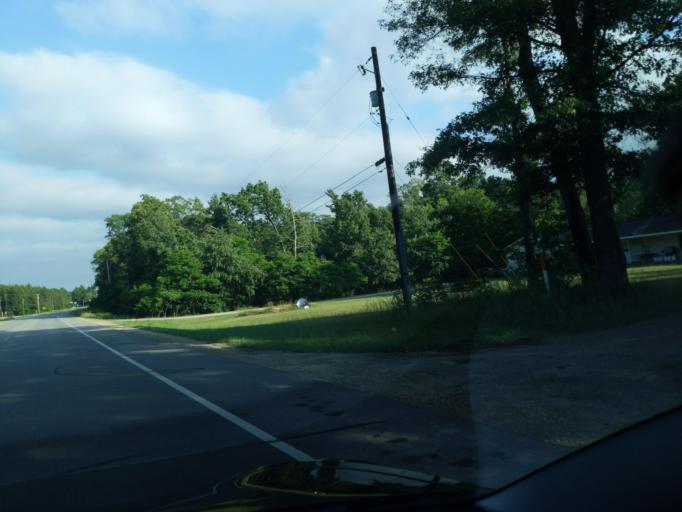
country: US
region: Michigan
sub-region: Muskegon County
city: Lakewood Club
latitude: 43.3878
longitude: -86.2925
